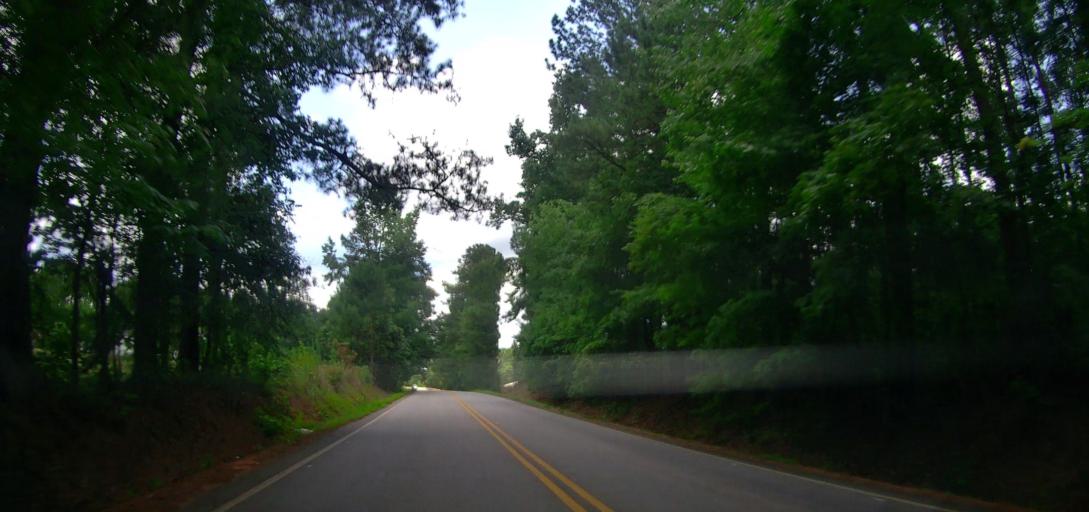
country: US
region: Georgia
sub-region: Troup County
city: Hogansville
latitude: 33.1228
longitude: -84.8161
